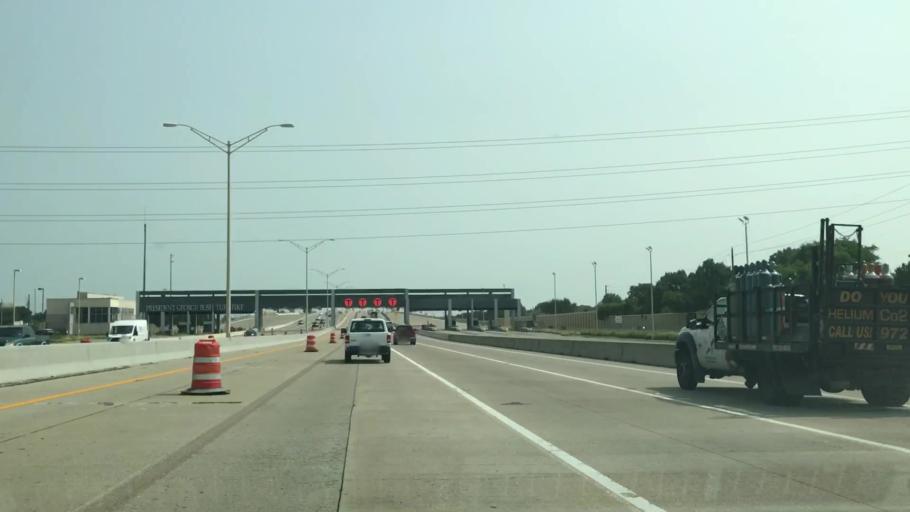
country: US
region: Texas
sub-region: Collin County
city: Plano
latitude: 32.9913
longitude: -96.6679
